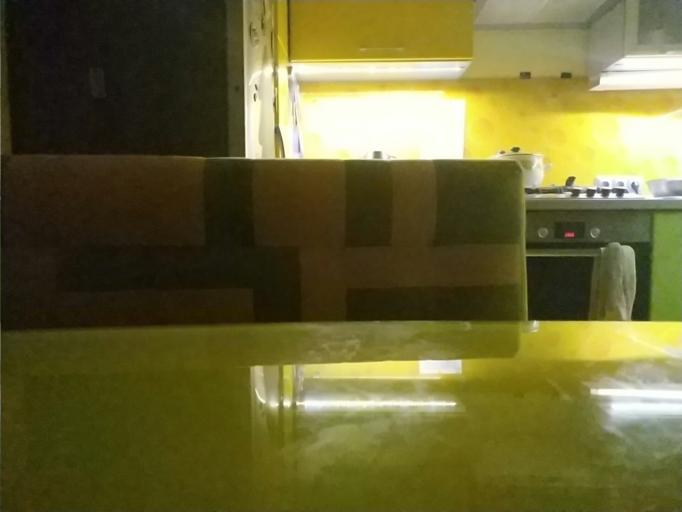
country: RU
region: Republic of Karelia
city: Pyaozerskiy
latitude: 65.6736
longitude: 30.5308
